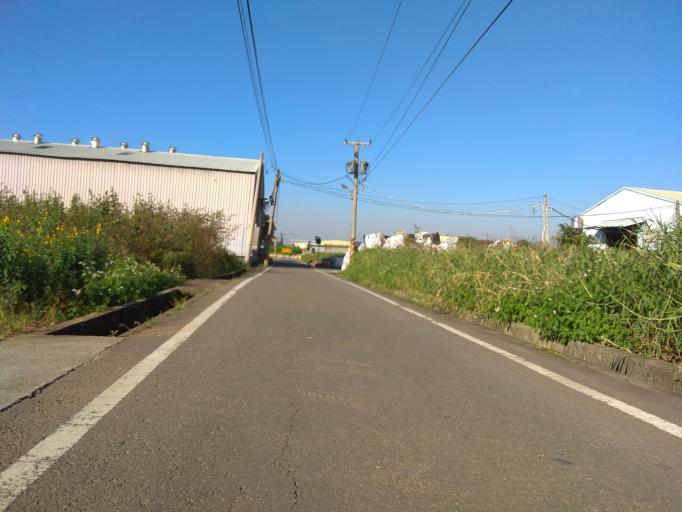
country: TW
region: Taiwan
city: Taoyuan City
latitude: 25.0088
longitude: 121.2264
